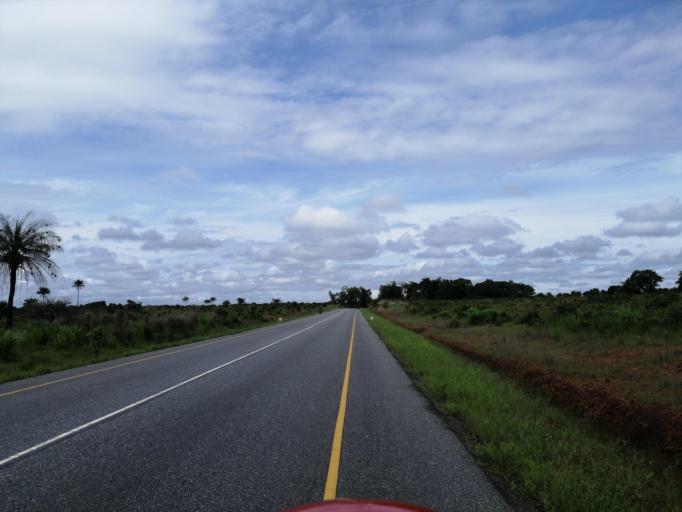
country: SL
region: Northern Province
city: Port Loko
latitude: 8.7324
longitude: -12.9497
